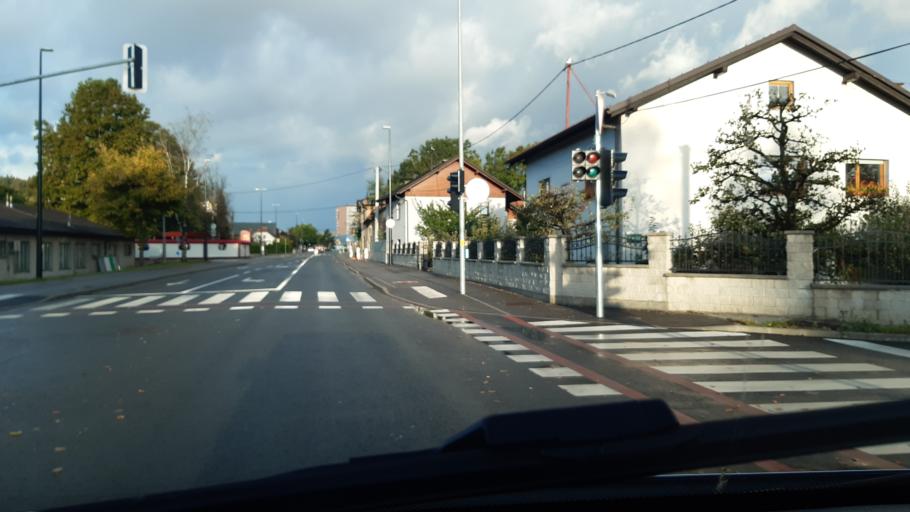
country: SI
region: Skofljica
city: Lavrica
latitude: 46.0466
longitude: 14.5534
